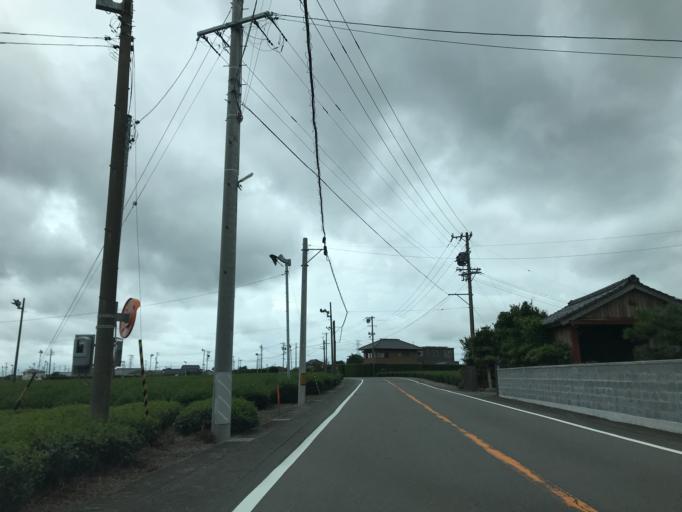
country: JP
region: Shizuoka
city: Sagara
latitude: 34.7342
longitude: 138.1409
